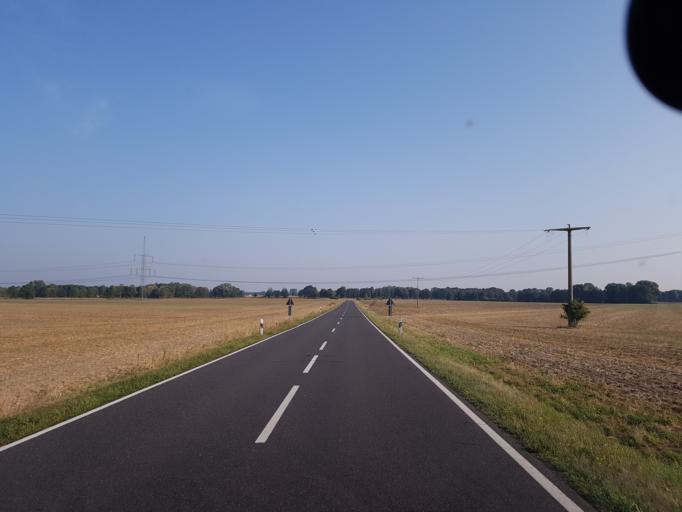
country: DE
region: Brandenburg
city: Finsterwalde
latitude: 51.6489
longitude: 13.7349
